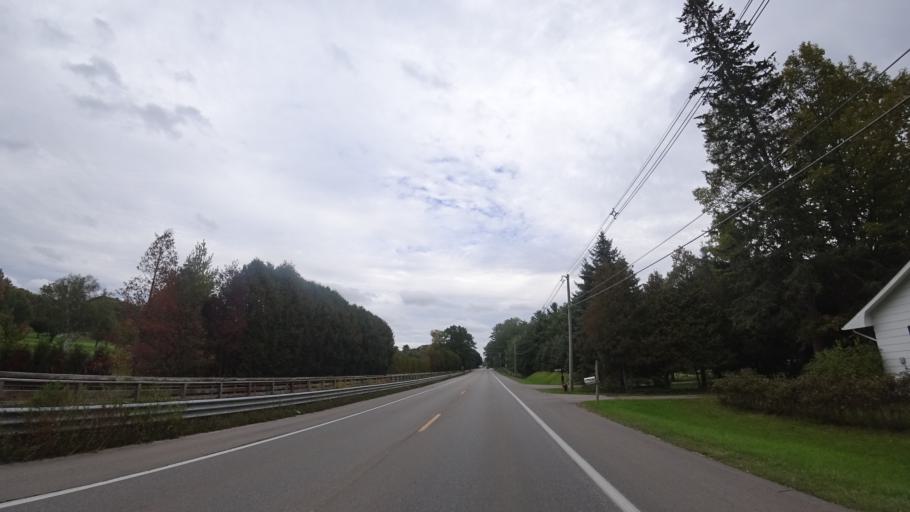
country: US
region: Michigan
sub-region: Emmet County
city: Harbor Springs
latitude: 45.4315
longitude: -84.9610
